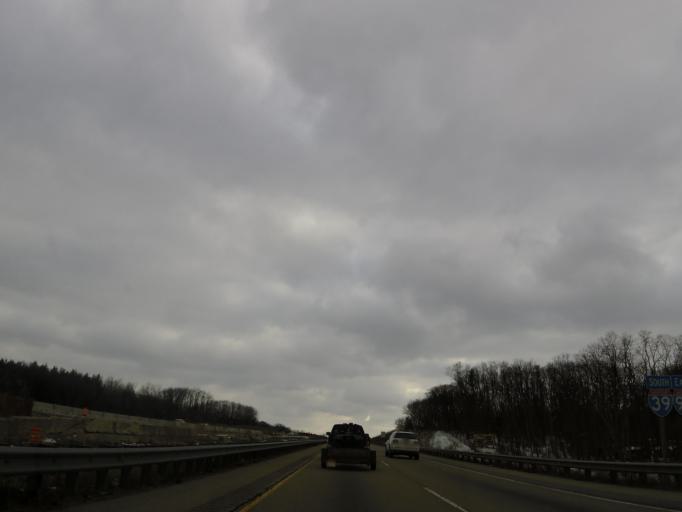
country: US
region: Wisconsin
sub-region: Rock County
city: Edgerton
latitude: 42.8283
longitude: -89.0260
